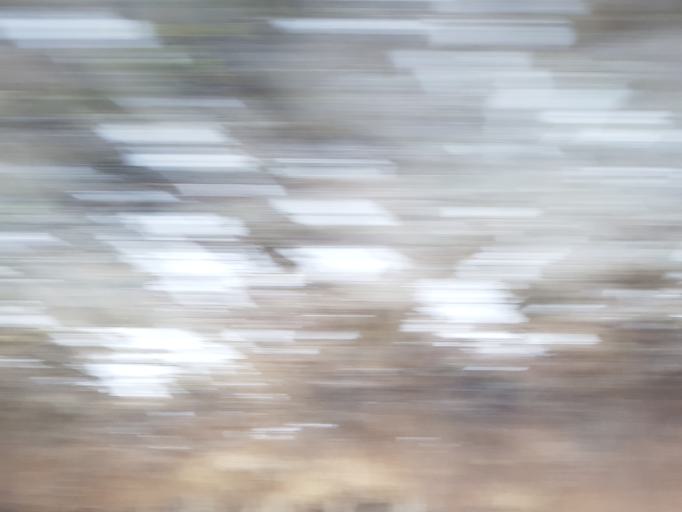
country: NO
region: Sor-Trondelag
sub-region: Midtre Gauldal
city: Storen
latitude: 62.9793
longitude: 10.2348
